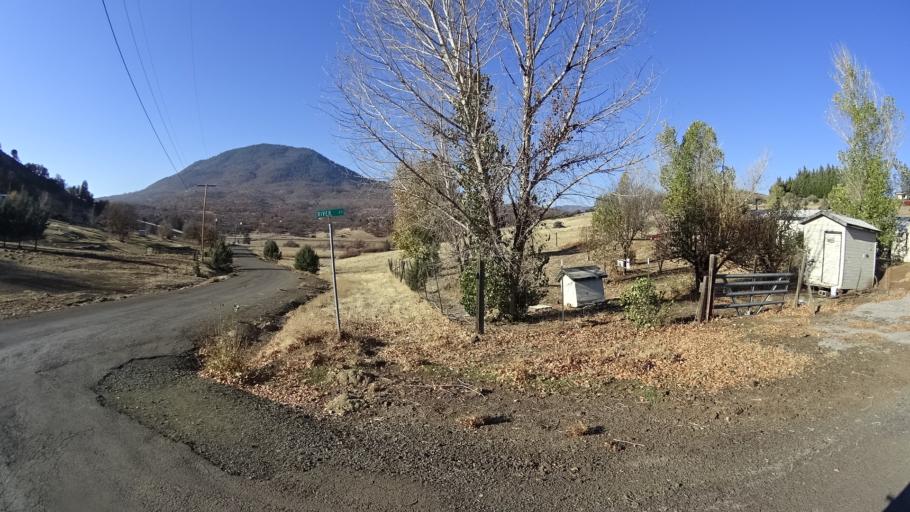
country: US
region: California
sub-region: Siskiyou County
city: Montague
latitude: 41.8945
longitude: -122.4791
